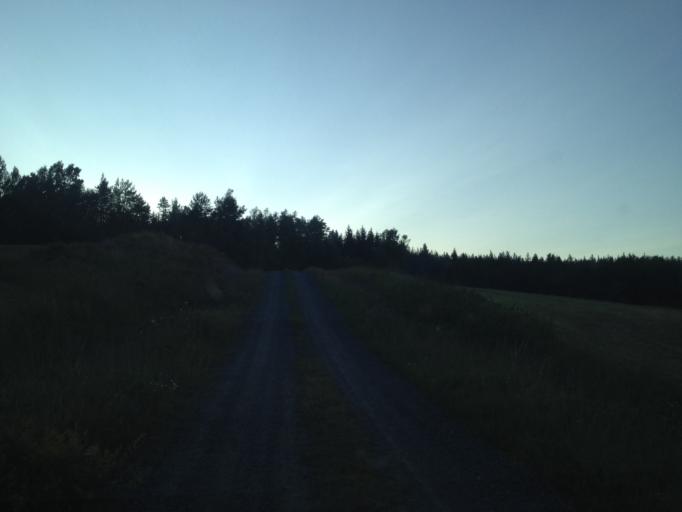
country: SE
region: Kalmar
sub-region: Vasterviks Kommun
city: Overum
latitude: 58.0207
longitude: 16.1193
